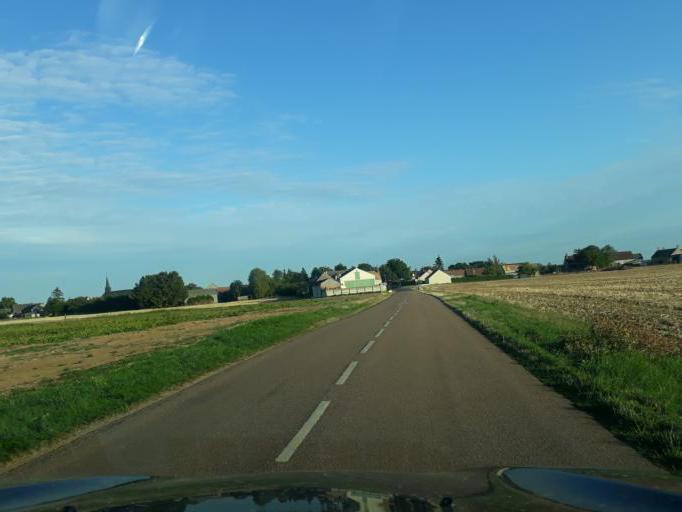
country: FR
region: Centre
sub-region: Departement du Loir-et-Cher
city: Ouzouer-le-Marche
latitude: 47.9660
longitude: 1.5437
